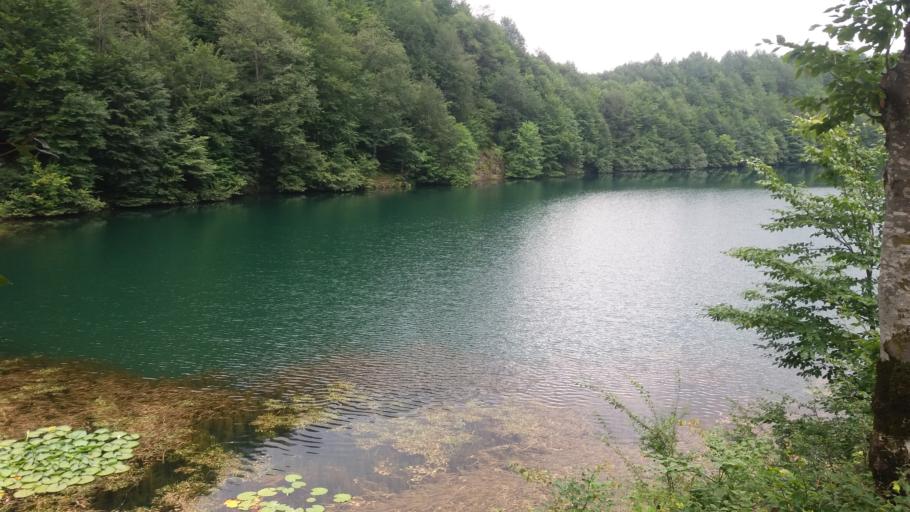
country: TR
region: Ordu
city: Golkoy
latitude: 40.6291
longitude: 37.5463
